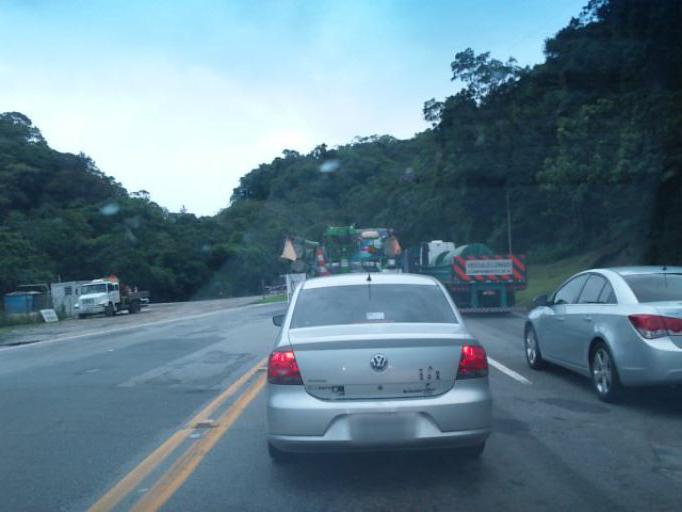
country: BR
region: Sao Paulo
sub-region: Juquitiba
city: Juquitiba
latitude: -24.0517
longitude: -47.2127
